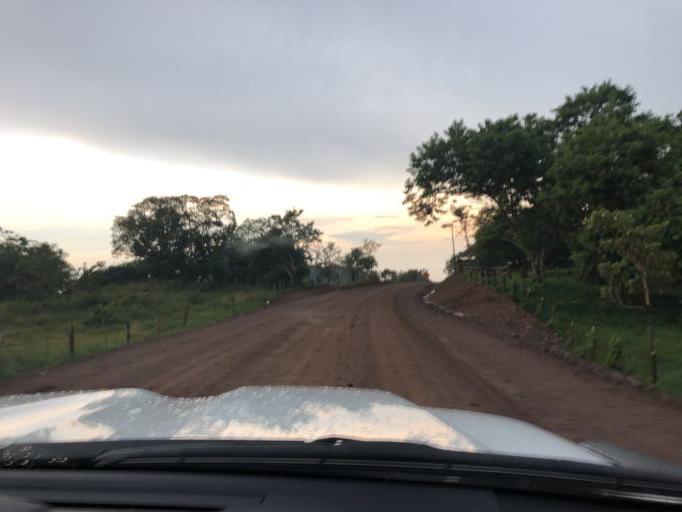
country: NI
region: Chontales
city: La Libertad
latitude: 12.1901
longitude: -85.1745
